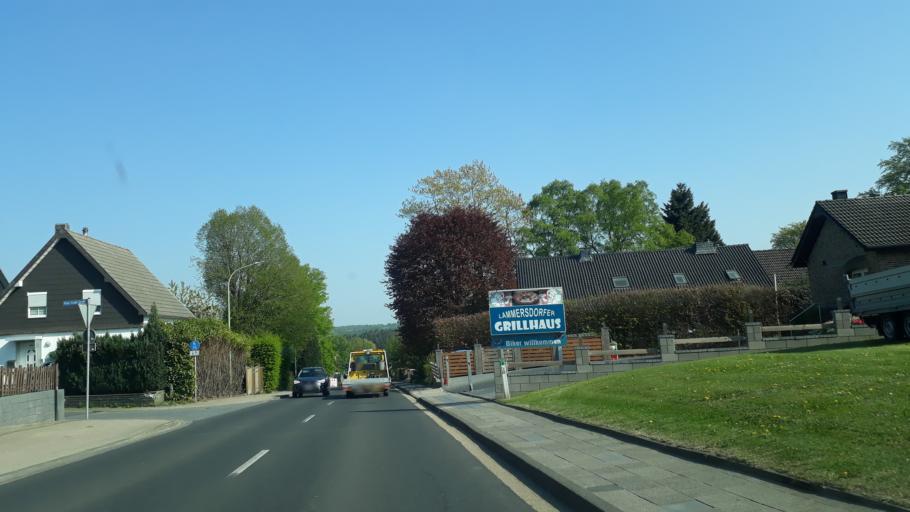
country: DE
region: North Rhine-Westphalia
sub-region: Regierungsbezirk Koln
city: Simmerath
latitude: 50.6311
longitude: 6.2821
